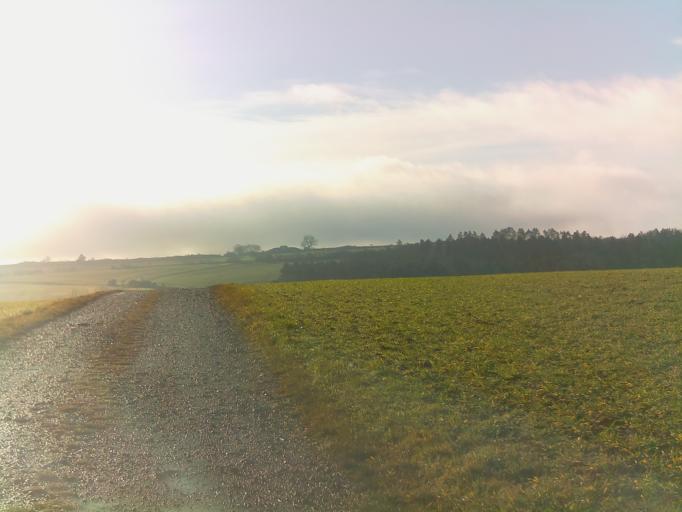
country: DE
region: Thuringia
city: Milda
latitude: 50.8551
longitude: 11.4039
